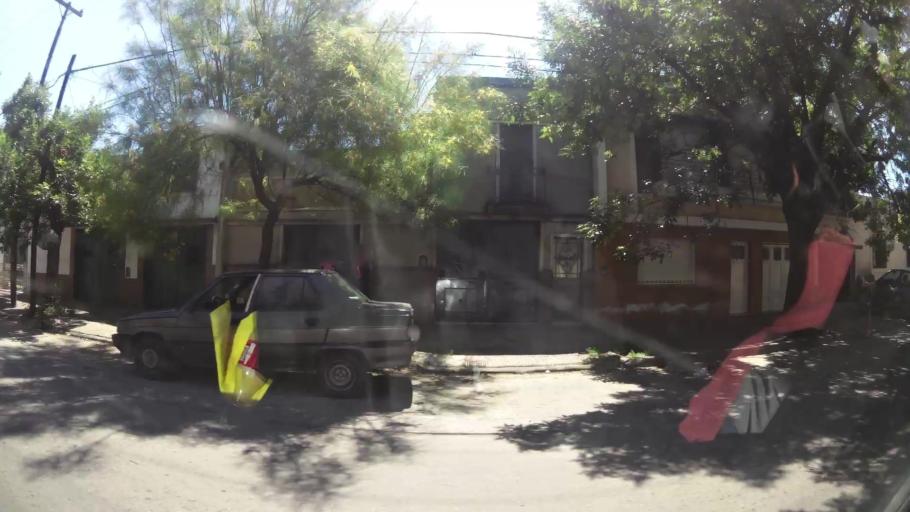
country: AR
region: Cordoba
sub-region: Departamento de Capital
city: Cordoba
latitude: -31.3928
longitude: -64.1919
